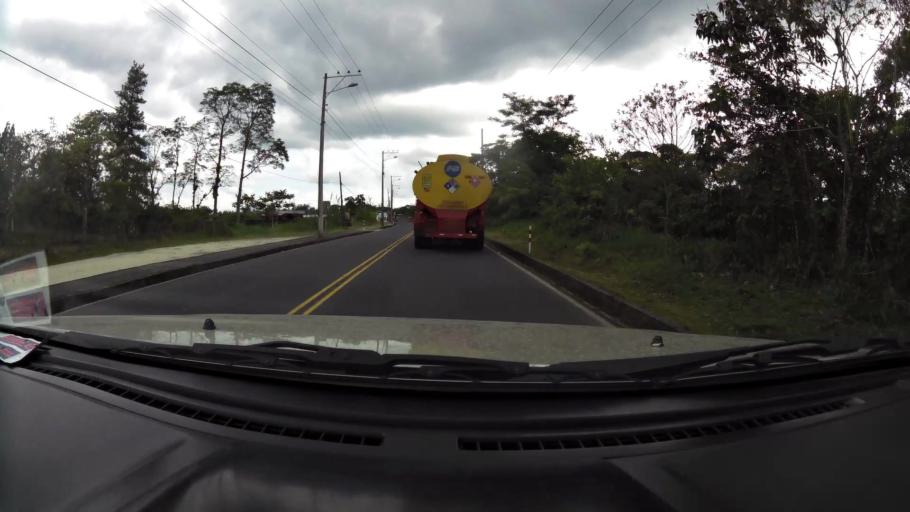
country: EC
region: Pastaza
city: Puyo
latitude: -1.4546
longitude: -78.1217
